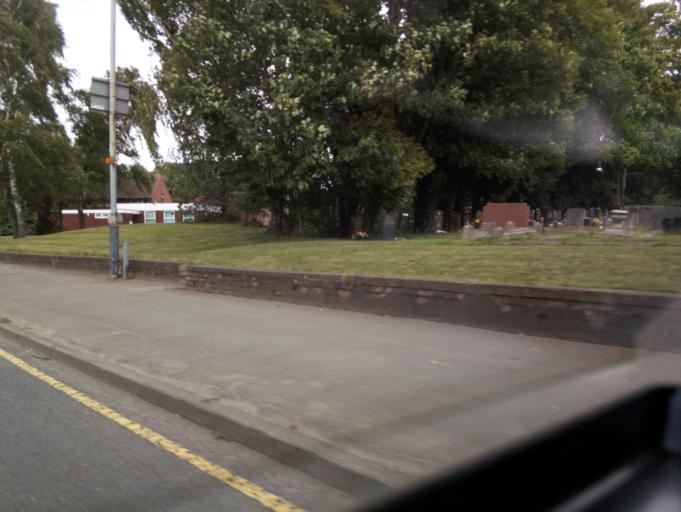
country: GB
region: England
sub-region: Warwickshire
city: Nuneaton
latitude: 52.5177
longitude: -1.4672
